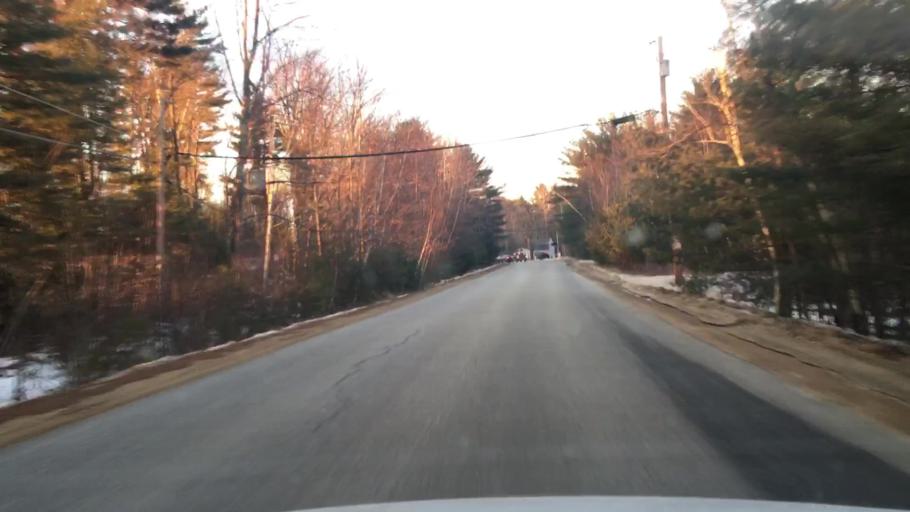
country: US
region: Maine
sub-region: York County
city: Lebanon
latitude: 43.3790
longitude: -70.8776
